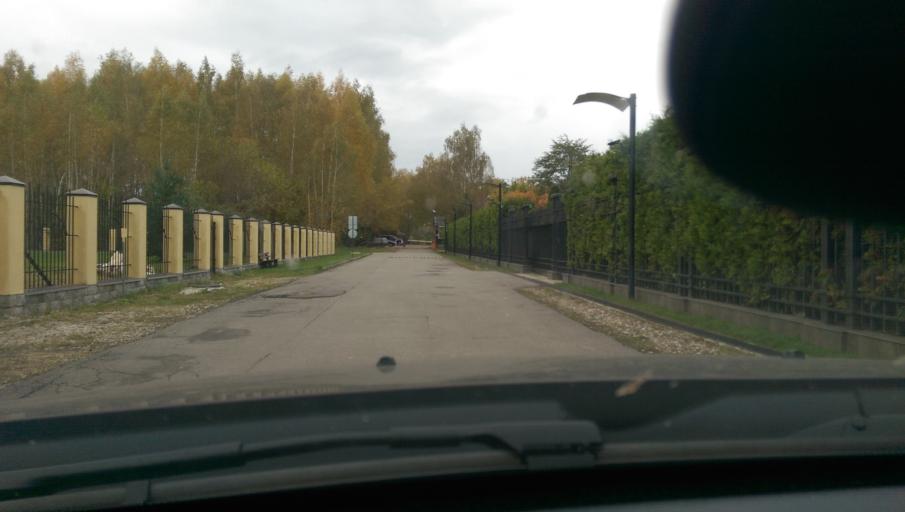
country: RU
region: Moskovskaya
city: Pirogovskiy
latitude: 56.0506
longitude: 37.6773
